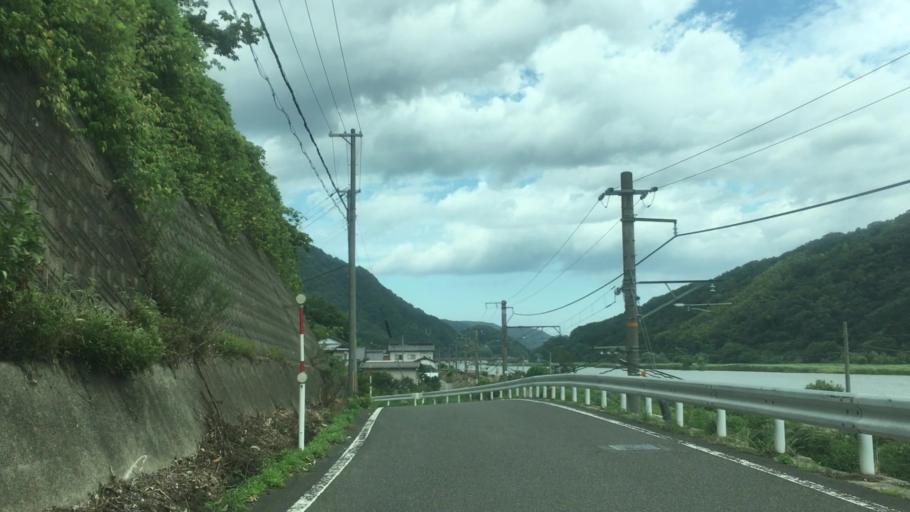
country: JP
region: Hyogo
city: Toyooka
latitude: 35.5948
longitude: 134.8008
